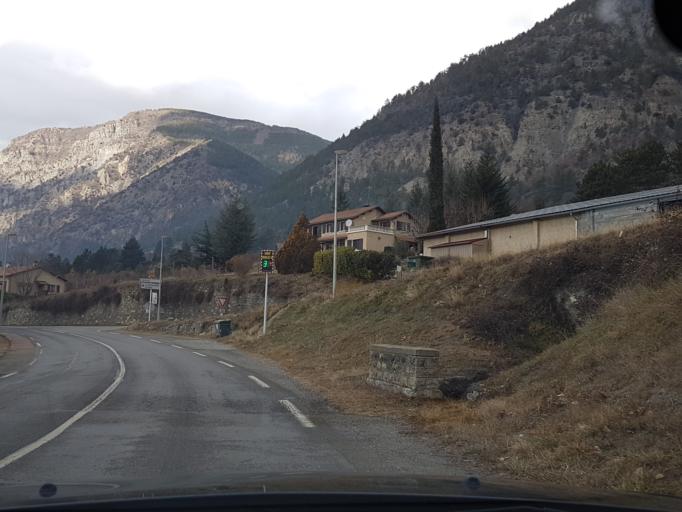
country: FR
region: Provence-Alpes-Cote d'Azur
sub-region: Departement des Hautes-Alpes
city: La Batie-Neuve
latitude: 44.4682
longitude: 6.1744
